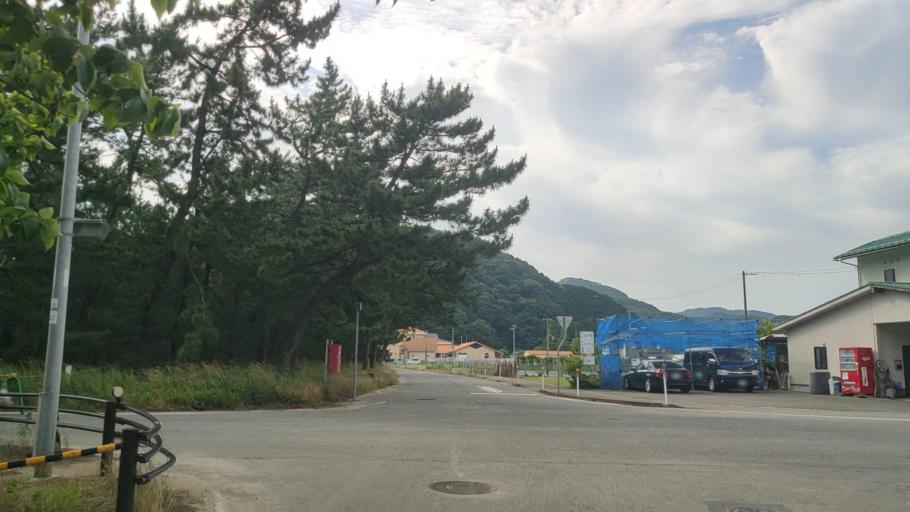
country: JP
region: Hyogo
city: Toyooka
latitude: 35.6428
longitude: 134.8368
